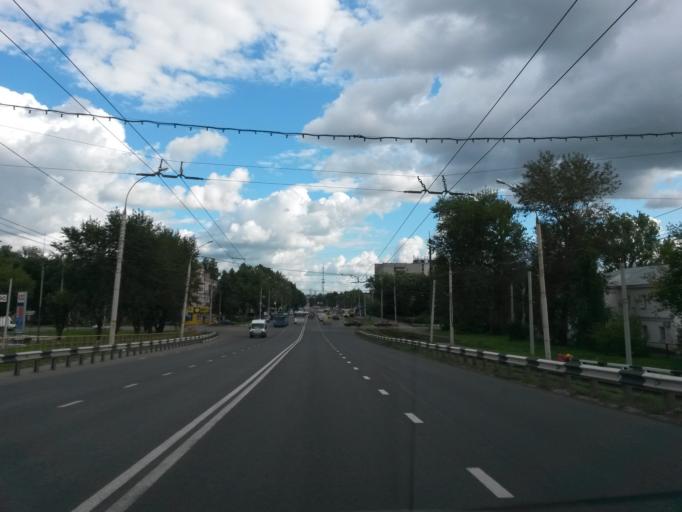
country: RU
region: Jaroslavl
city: Yaroslavl
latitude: 57.6423
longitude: 39.8549
